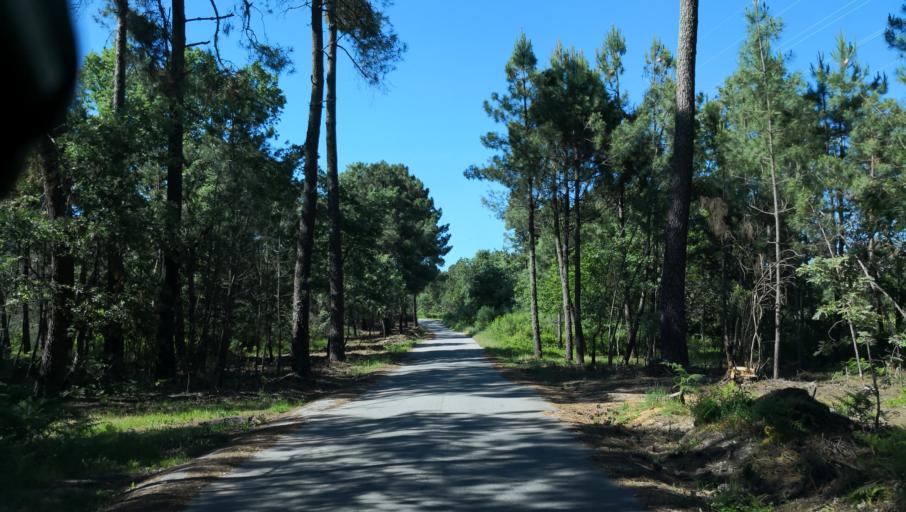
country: PT
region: Vila Real
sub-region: Vila Real
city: Vila Real
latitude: 41.2981
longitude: -7.6690
